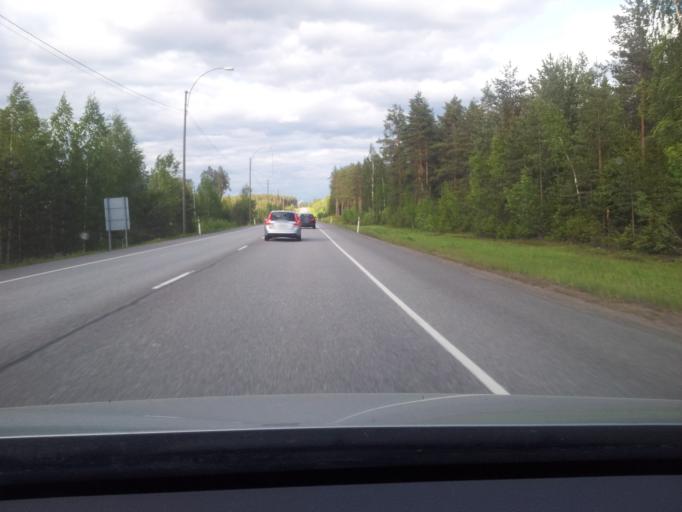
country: FI
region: South Karelia
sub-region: Lappeenranta
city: Taavetti
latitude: 60.9235
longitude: 27.5503
